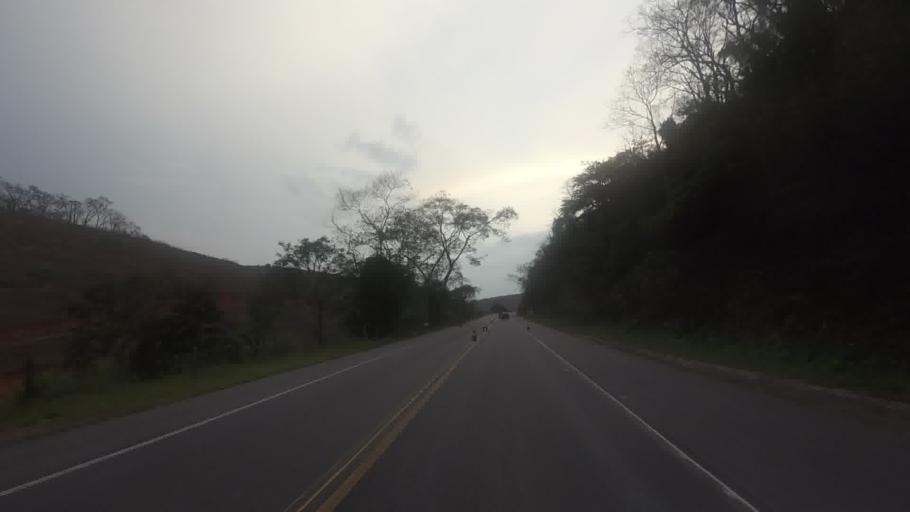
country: BR
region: Rio de Janeiro
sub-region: Carmo
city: Carmo
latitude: -21.8104
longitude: -42.5870
